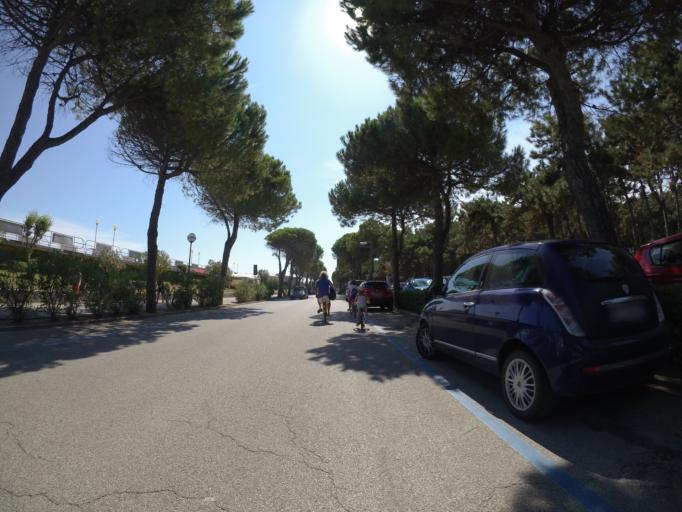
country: IT
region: Friuli Venezia Giulia
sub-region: Provincia di Udine
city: Lignano Sabbiadoro
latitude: 45.6705
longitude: 13.1165
